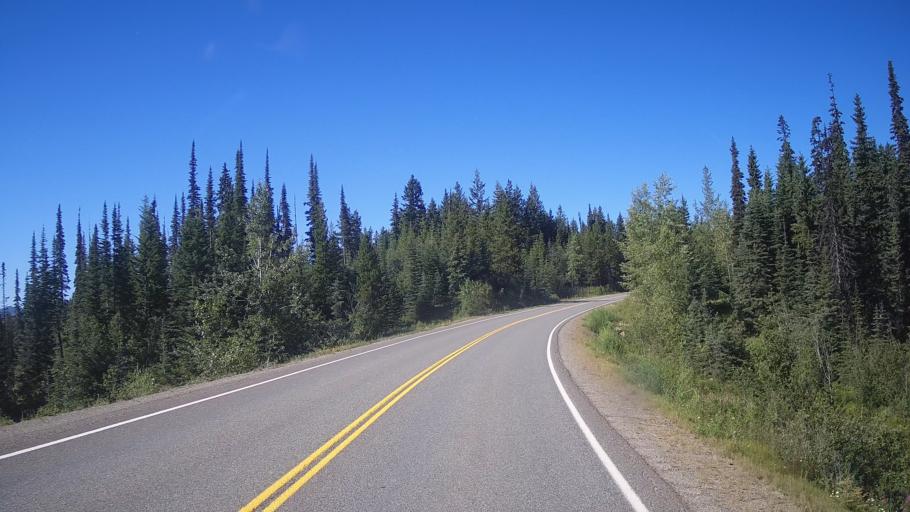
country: CA
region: British Columbia
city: Kamloops
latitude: 51.4992
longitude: -120.3606
